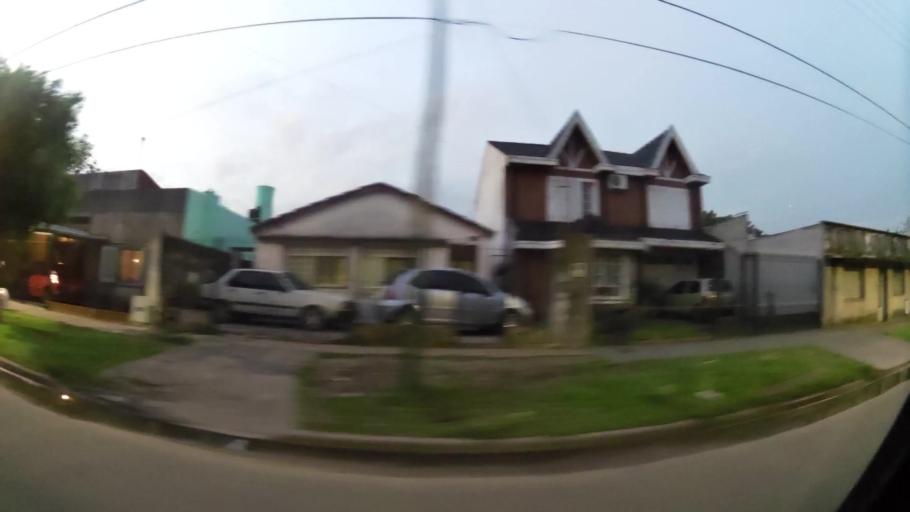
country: AR
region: Buenos Aires
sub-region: Partido de Lomas de Zamora
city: Lomas de Zamora
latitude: -34.7483
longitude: -58.3615
